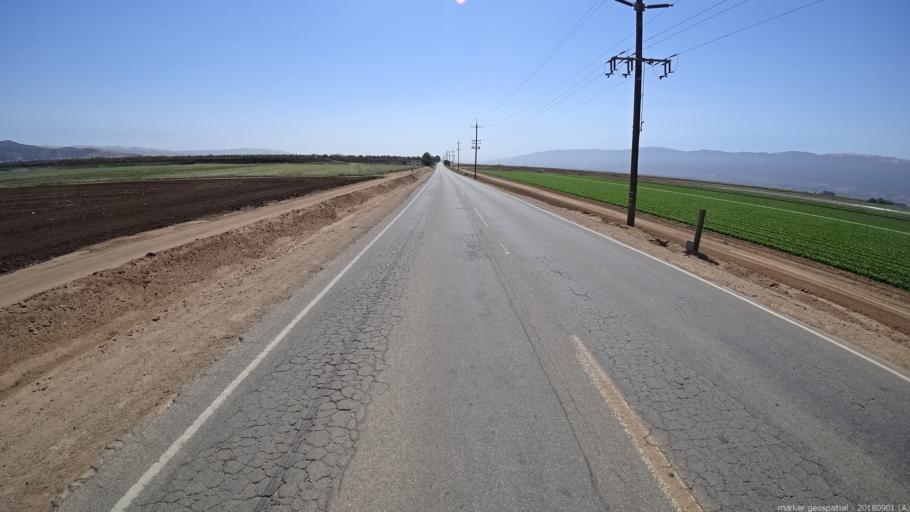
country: US
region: California
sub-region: Monterey County
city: Chualar
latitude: 36.5804
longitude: -121.4973
